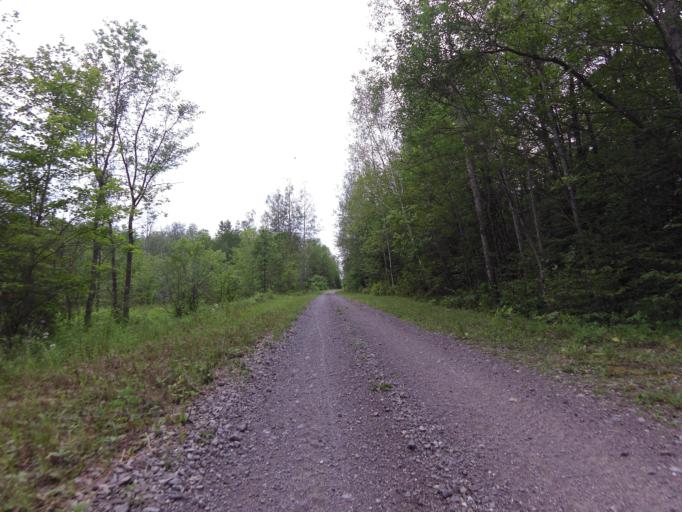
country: CA
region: Ontario
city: Perth
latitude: 44.8165
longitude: -76.5938
